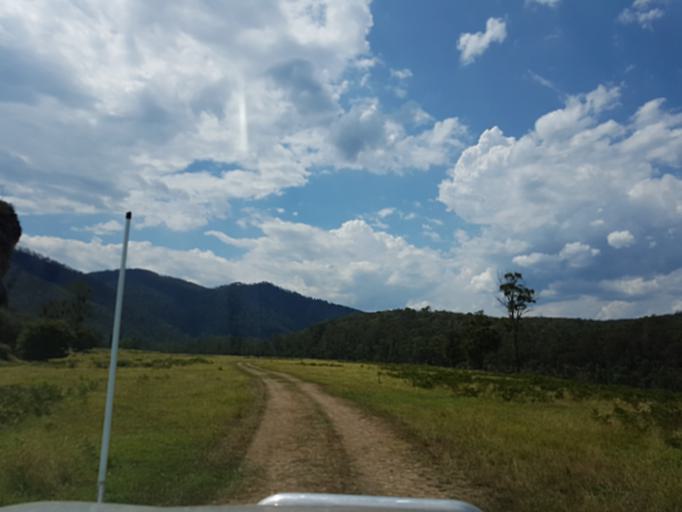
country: AU
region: Victoria
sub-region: East Gippsland
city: Lakes Entrance
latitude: -37.4025
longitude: 148.3336
